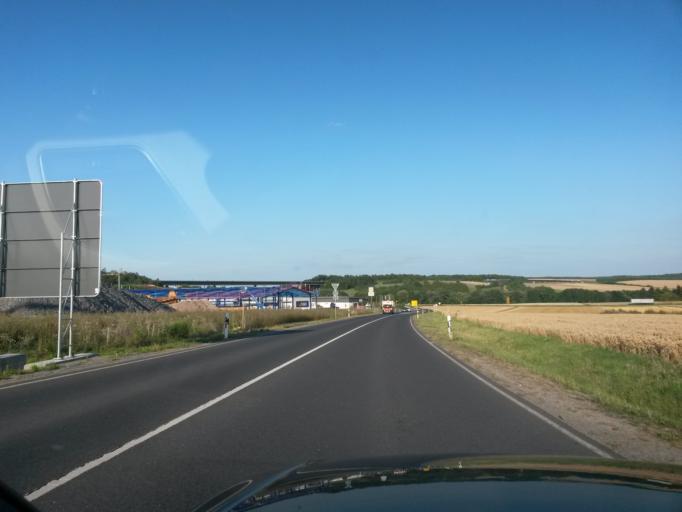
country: DE
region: Bavaria
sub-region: Regierungsbezirk Unterfranken
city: Estenfeld
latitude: 49.8405
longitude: 10.0117
